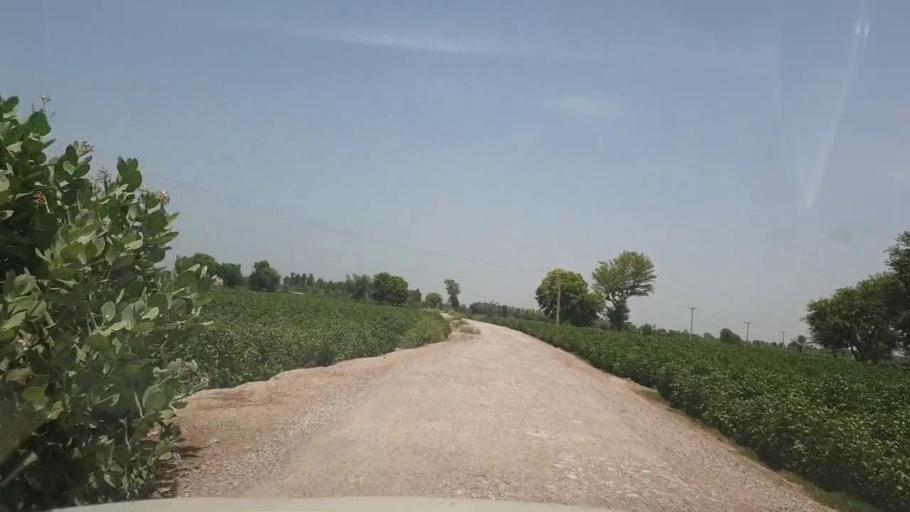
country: PK
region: Sindh
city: Bozdar
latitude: 27.1623
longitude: 68.6189
